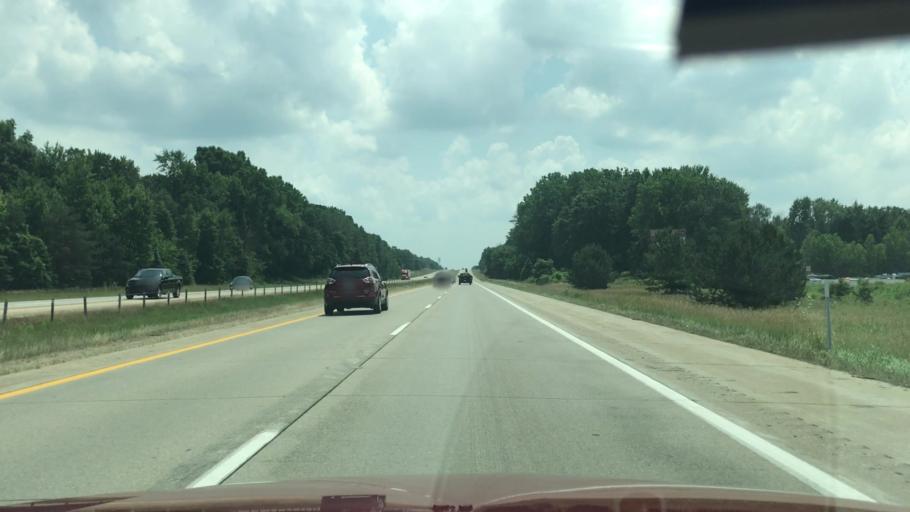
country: US
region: Michigan
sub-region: Allegan County
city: Otsego
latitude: 42.5148
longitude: -85.6559
